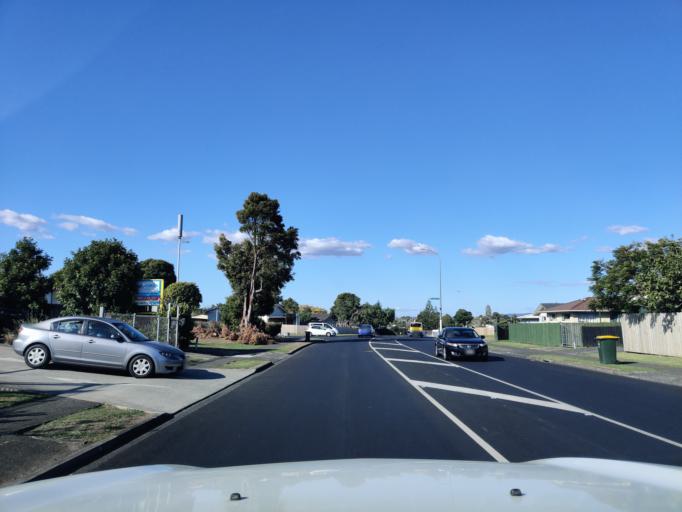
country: NZ
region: Auckland
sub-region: Auckland
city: Takanini
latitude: -37.0376
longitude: 174.8892
